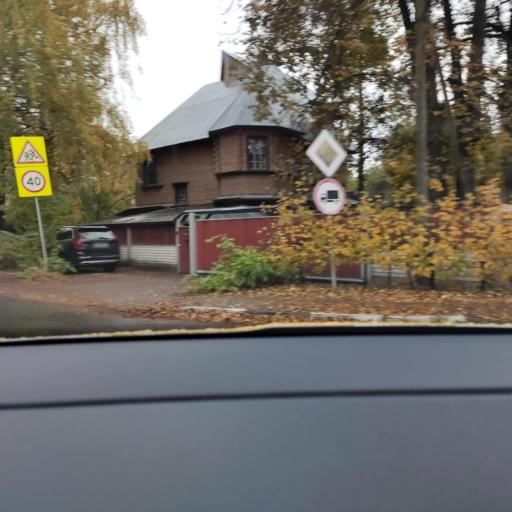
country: RU
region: Moskovskaya
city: Ivanteyevka
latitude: 55.9703
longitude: 37.9443
